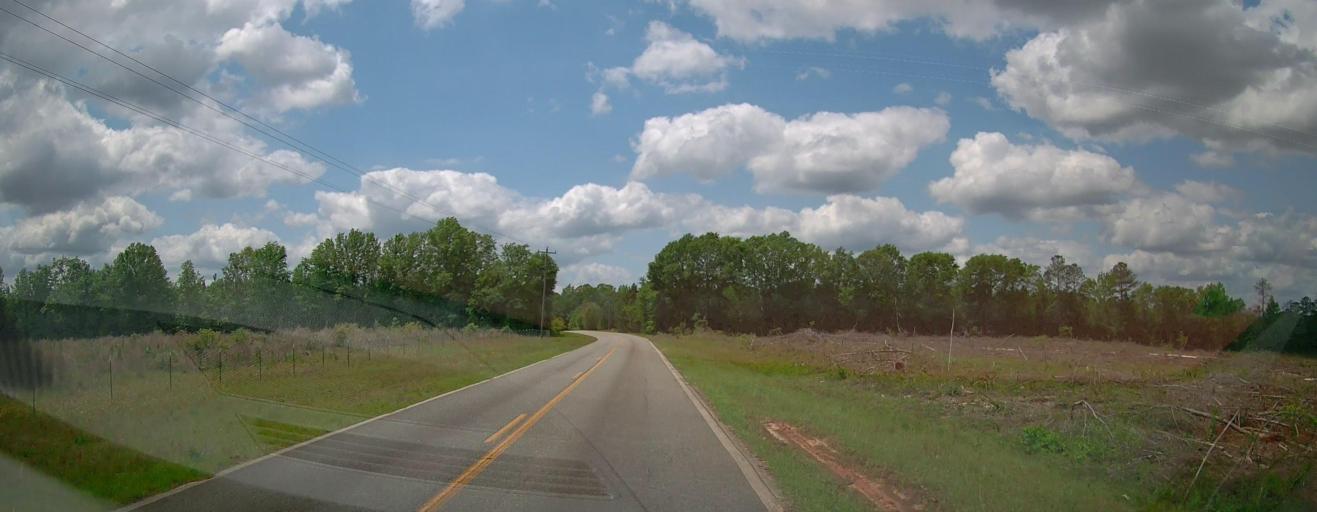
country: US
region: Georgia
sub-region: Laurens County
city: Dublin
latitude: 32.6290
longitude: -82.9836
